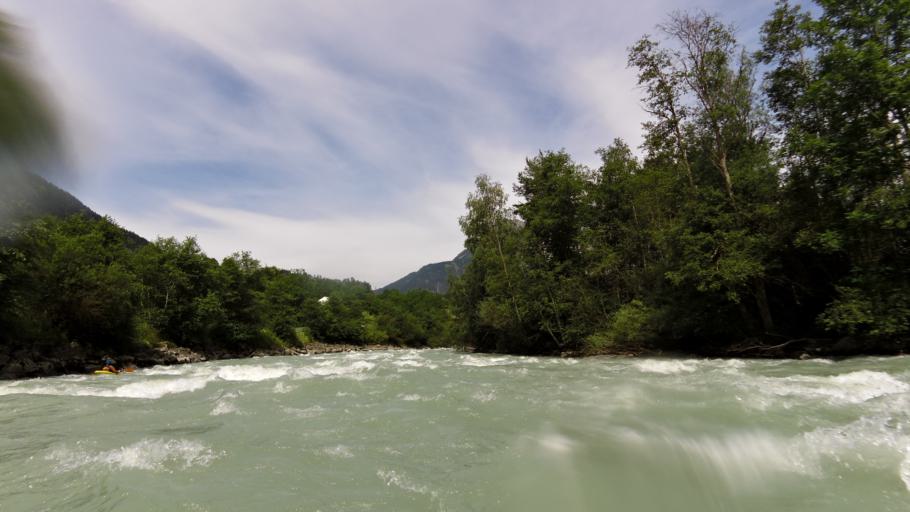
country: AT
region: Tyrol
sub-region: Politischer Bezirk Imst
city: Sautens
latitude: 47.2126
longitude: 10.8650
